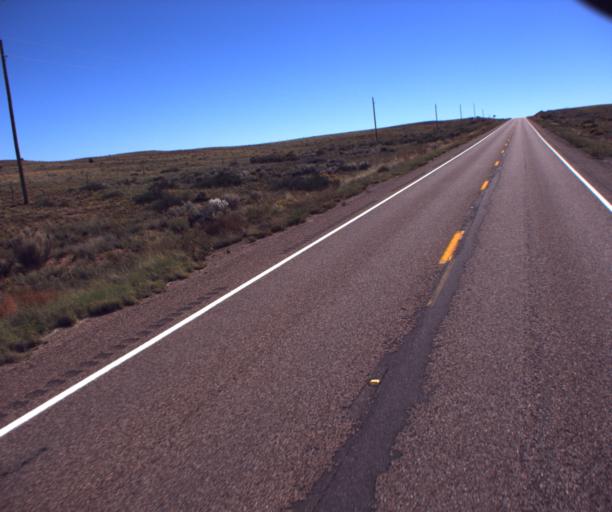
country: US
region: Arizona
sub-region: Apache County
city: Saint Johns
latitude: 34.5441
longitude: -109.4772
